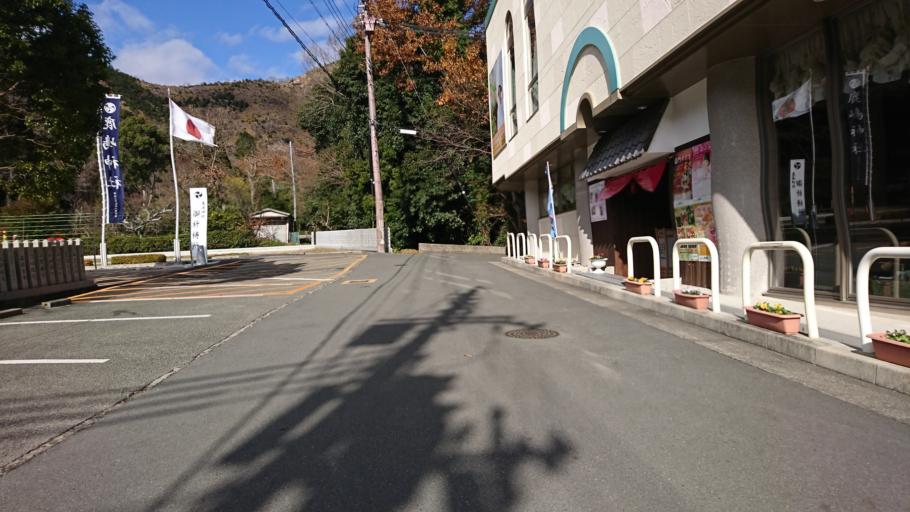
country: JP
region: Hyogo
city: Shirahamacho-usazakiminami
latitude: 34.8094
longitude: 134.7755
